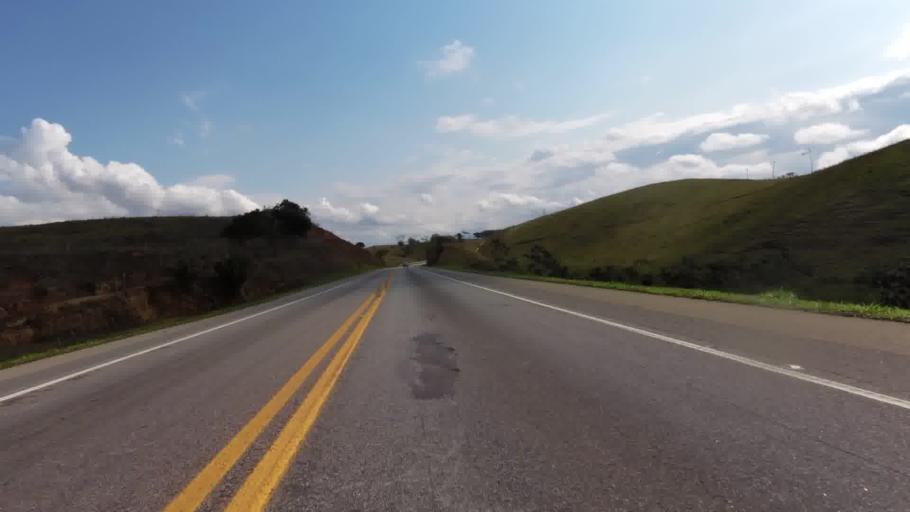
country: BR
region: Rio de Janeiro
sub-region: Macae
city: Macae
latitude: -22.2516
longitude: -41.8211
